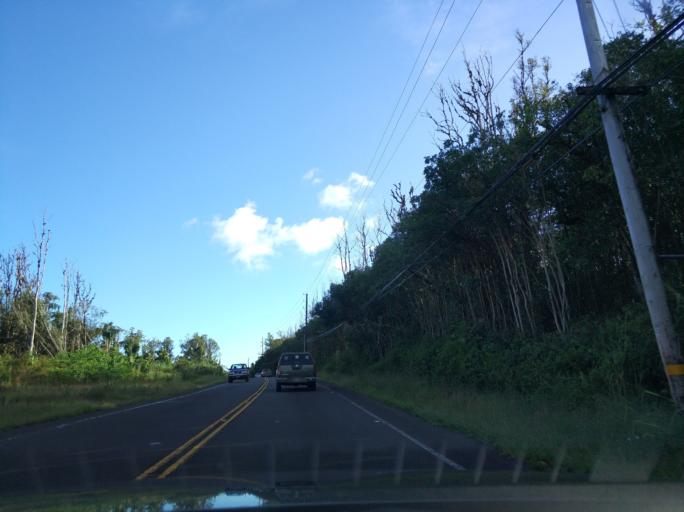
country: US
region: Hawaii
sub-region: Hawaii County
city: Leilani Estates
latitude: 19.4648
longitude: -154.9413
